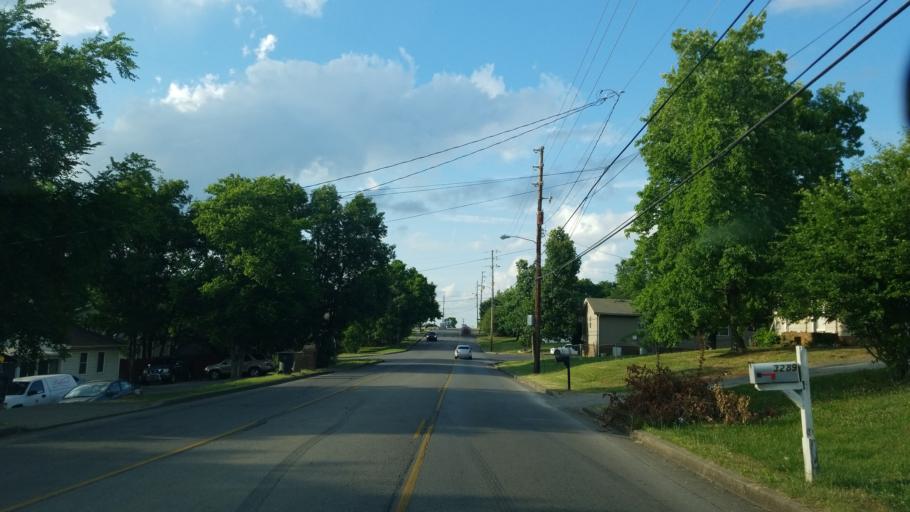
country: US
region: Tennessee
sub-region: Rutherford County
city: La Vergne
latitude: 36.0796
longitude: -86.6067
